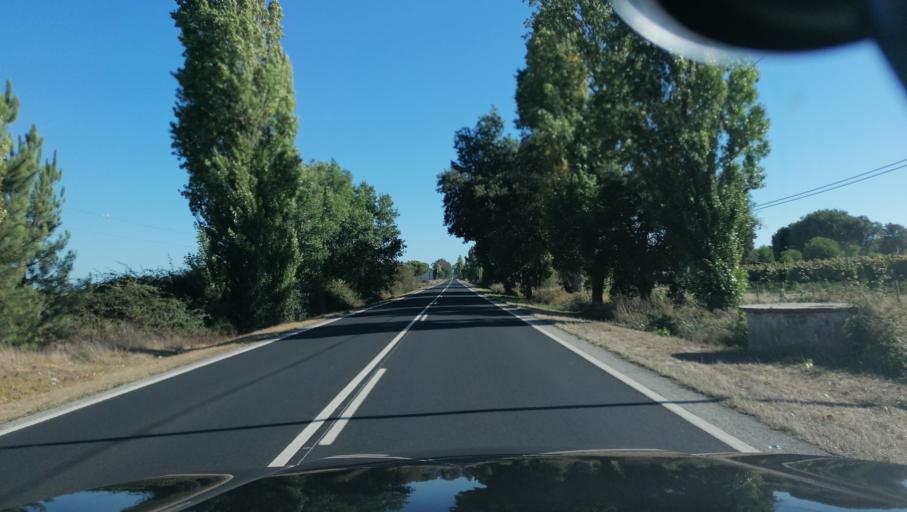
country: PT
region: Santarem
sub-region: Benavente
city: Poceirao
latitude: 38.8097
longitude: -8.8808
